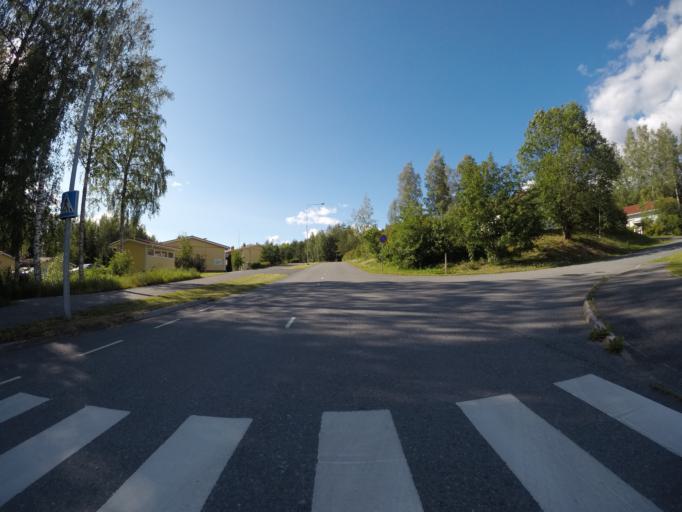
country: FI
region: Haeme
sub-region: Haemeenlinna
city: Haemeenlinna
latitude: 61.0213
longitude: 24.5194
